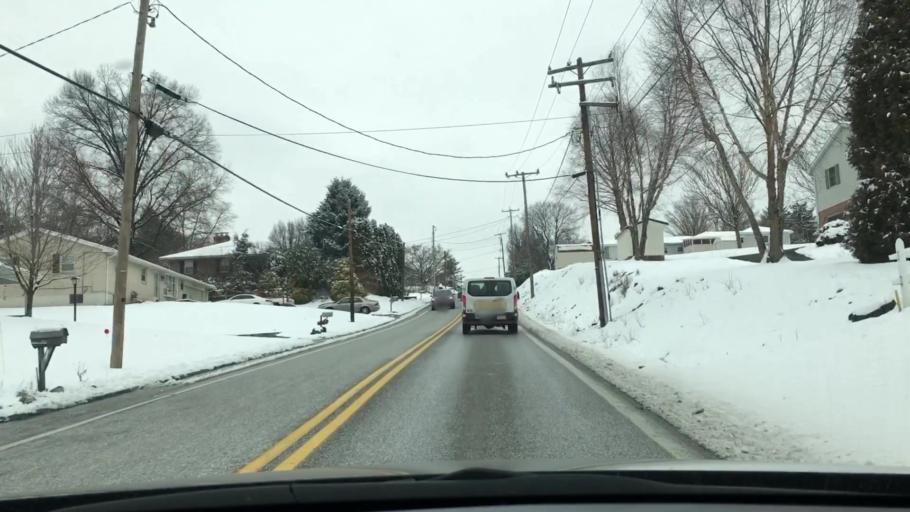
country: US
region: Pennsylvania
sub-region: York County
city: East York
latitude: 39.9851
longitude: -76.7072
